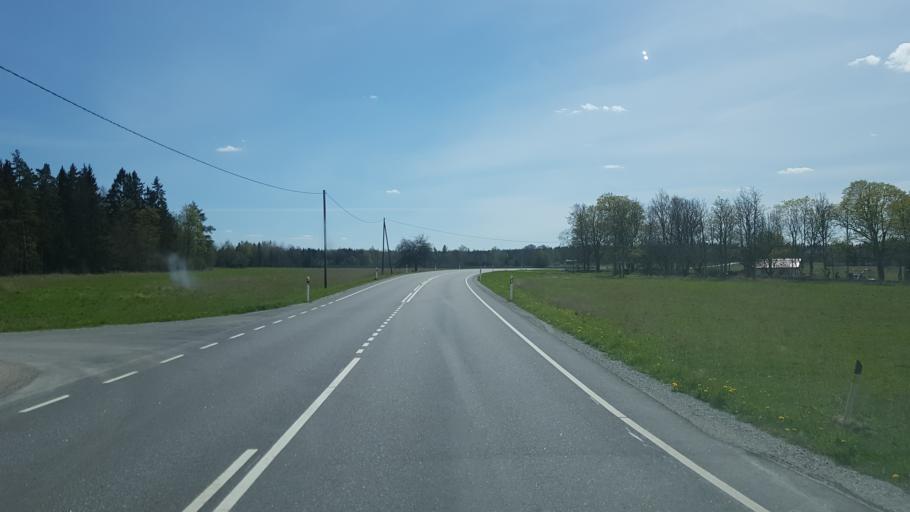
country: EE
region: Harju
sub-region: Paldiski linn
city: Paldiski
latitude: 59.2001
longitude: 24.0969
